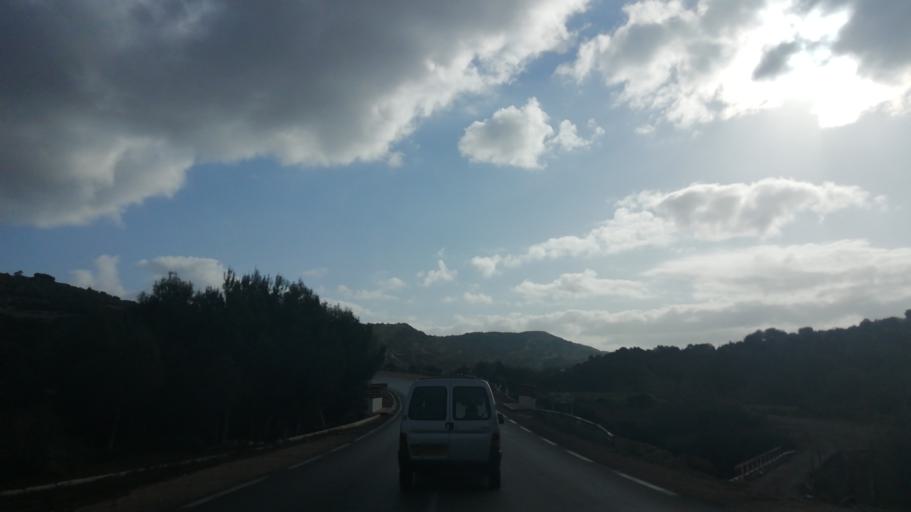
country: DZ
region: Relizane
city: Mazouna
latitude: 36.2375
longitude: 0.5404
